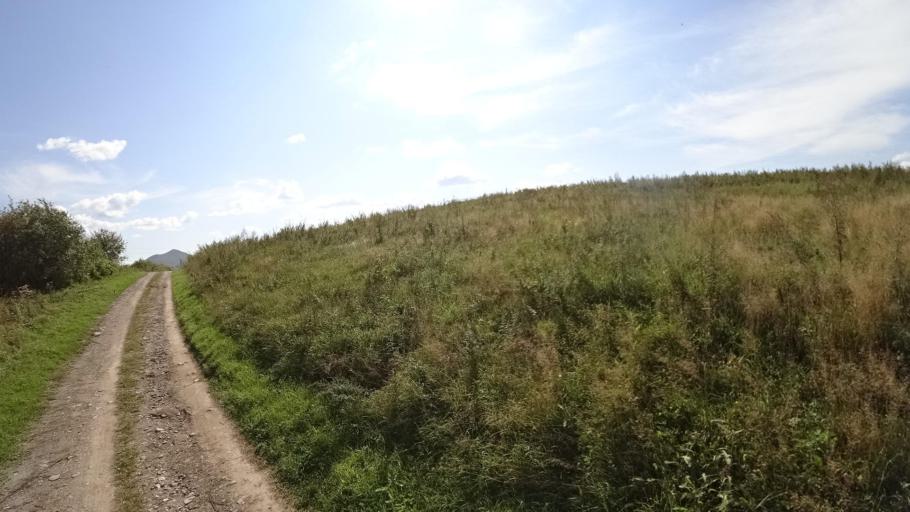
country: RU
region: Jewish Autonomous Oblast
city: Londoko
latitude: 49.0084
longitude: 131.8659
